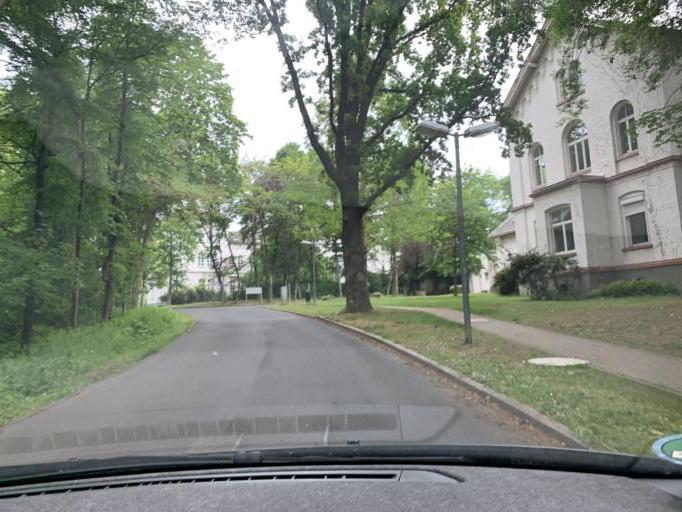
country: DE
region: North Rhine-Westphalia
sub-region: Regierungsbezirk Koln
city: Dueren
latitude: 50.8149
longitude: 6.4822
